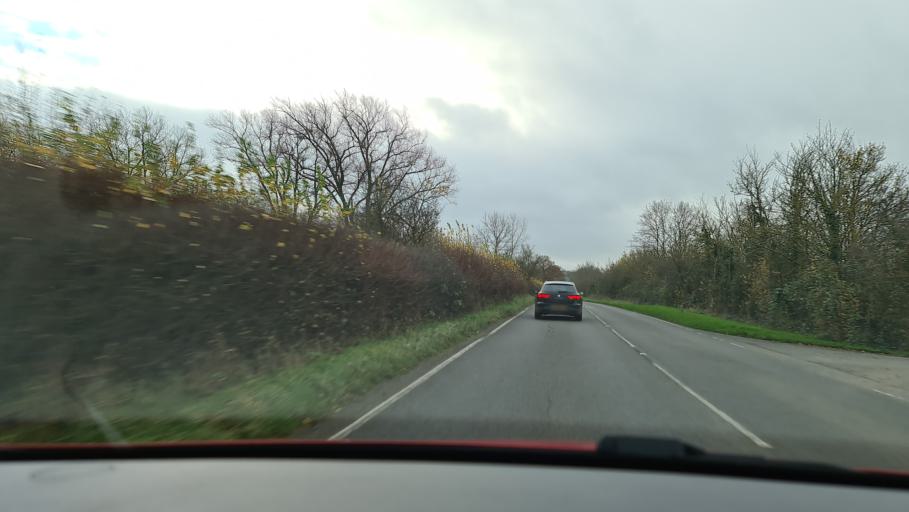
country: GB
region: England
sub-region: Oxfordshire
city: Bicester
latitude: 51.8461
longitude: -1.0889
